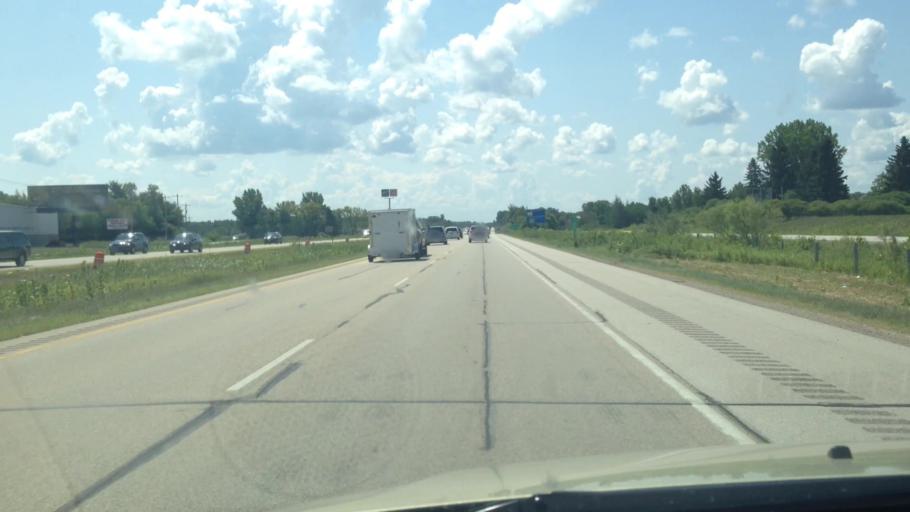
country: US
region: Wisconsin
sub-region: Brown County
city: Suamico
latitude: 44.6869
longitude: -88.0506
